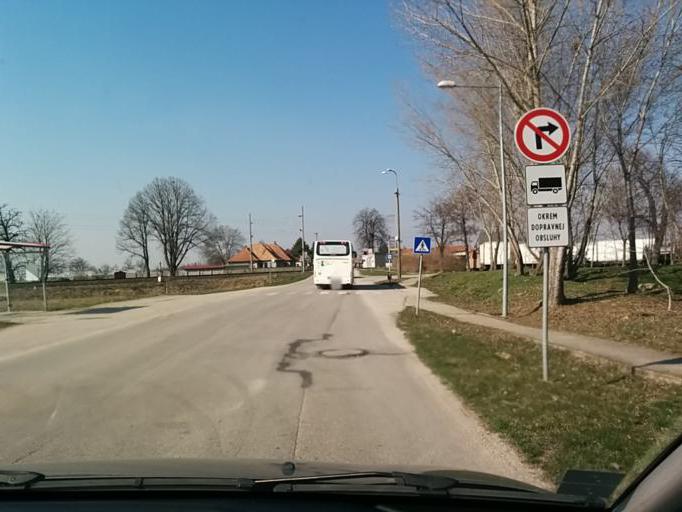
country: SK
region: Trnavsky
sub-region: Okres Galanta
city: Galanta
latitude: 48.2254
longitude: 17.7208
